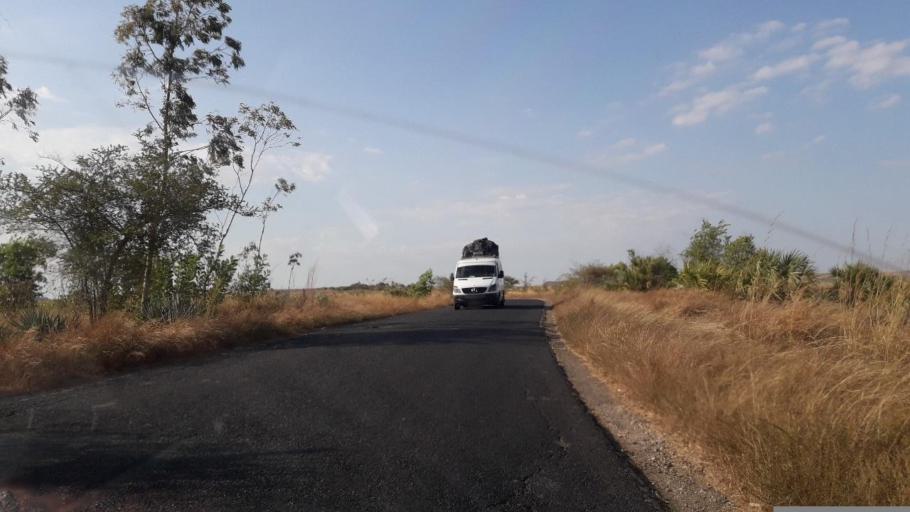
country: MG
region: Boeny
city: Marovoay
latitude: -15.8753
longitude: 46.5396
